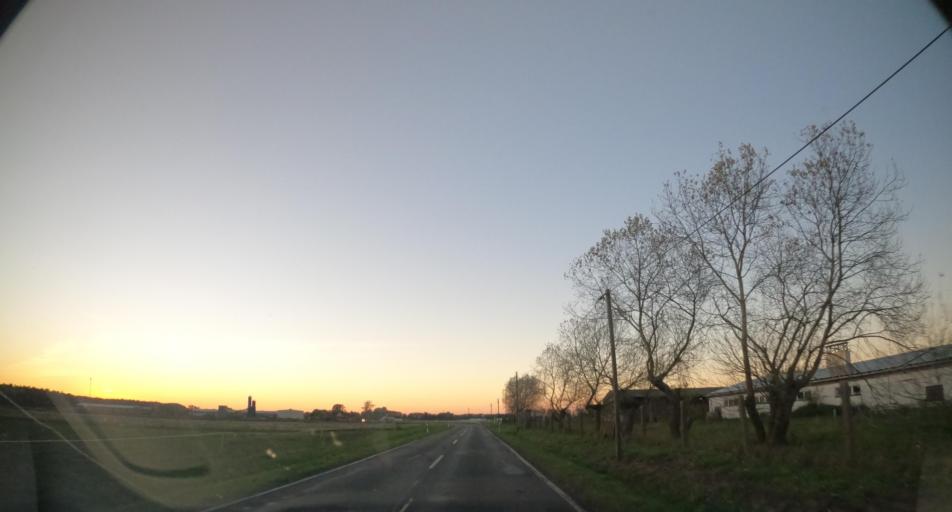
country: DE
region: Mecklenburg-Vorpommern
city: Ducherow
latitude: 53.7781
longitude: 13.8820
